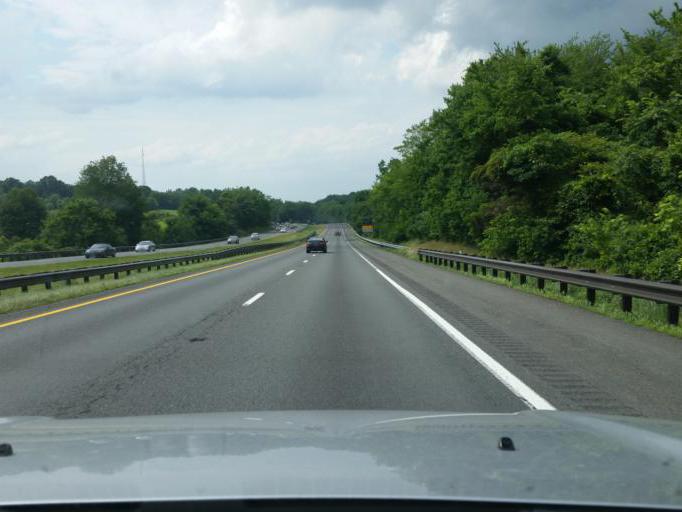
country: US
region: Maryland
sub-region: Montgomery County
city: Clarksburg
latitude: 39.2499
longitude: -77.3002
